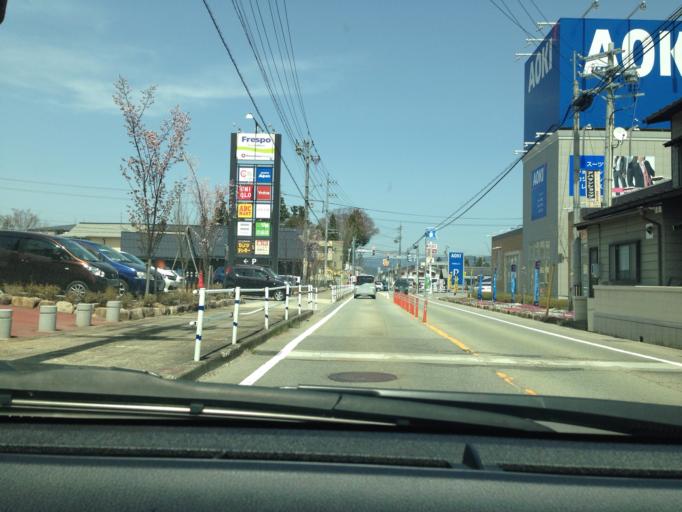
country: JP
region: Gifu
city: Takayama
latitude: 36.1330
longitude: 137.2557
